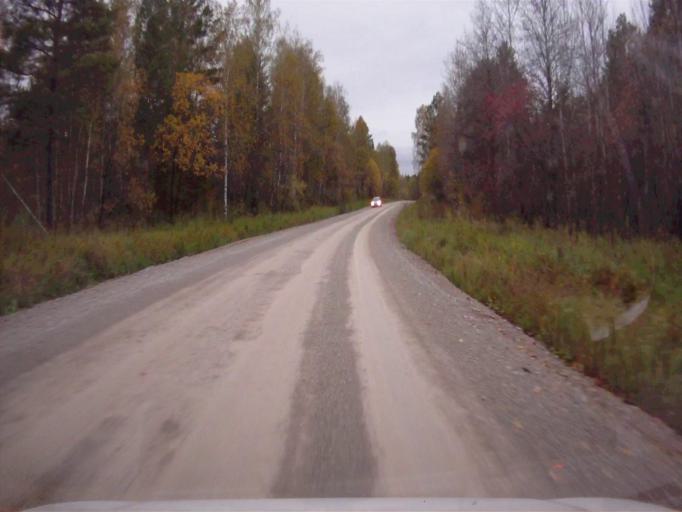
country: RU
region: Chelyabinsk
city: Nyazepetrovsk
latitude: 56.0631
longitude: 59.4443
